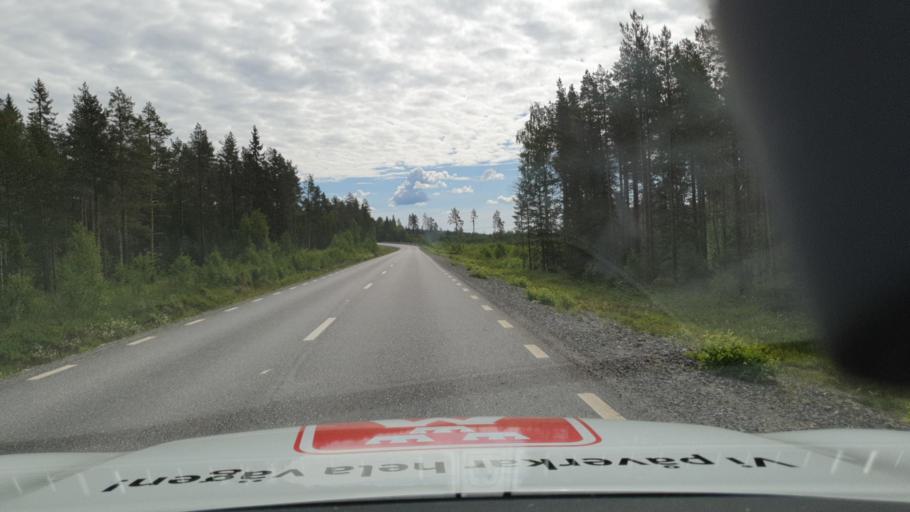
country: SE
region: Vaesterbotten
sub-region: Umea Kommun
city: Ersmark
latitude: 64.2520
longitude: 20.1408
